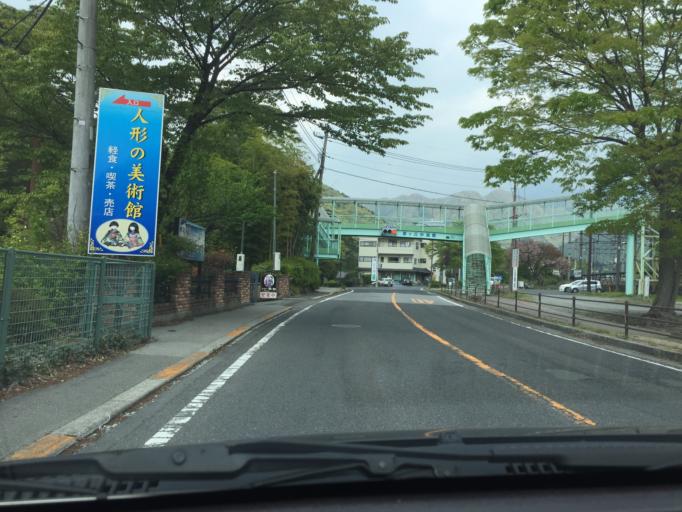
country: JP
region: Tochigi
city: Imaichi
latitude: 36.8417
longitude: 139.7225
